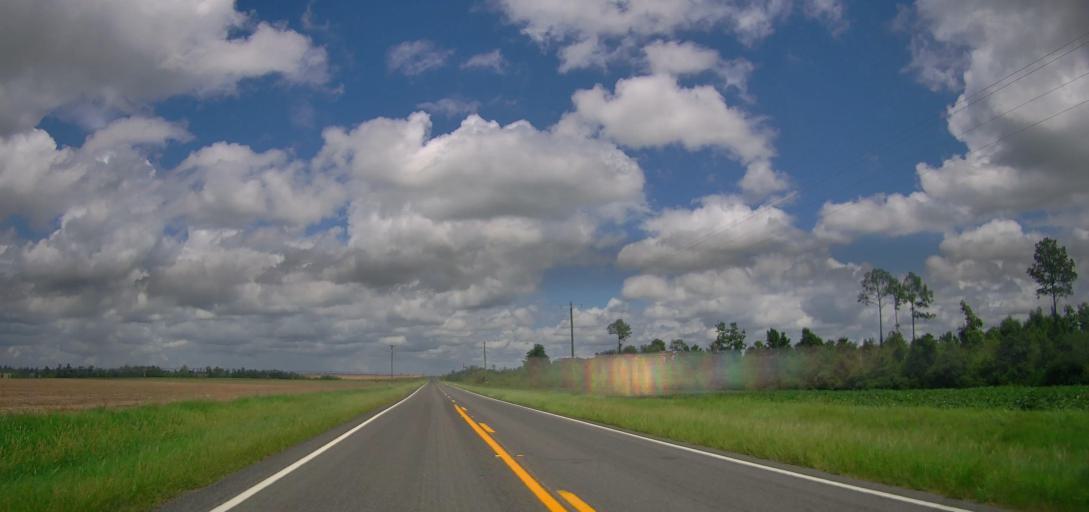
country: US
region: Georgia
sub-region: Turner County
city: Ashburn
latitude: 31.8103
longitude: -83.5720
